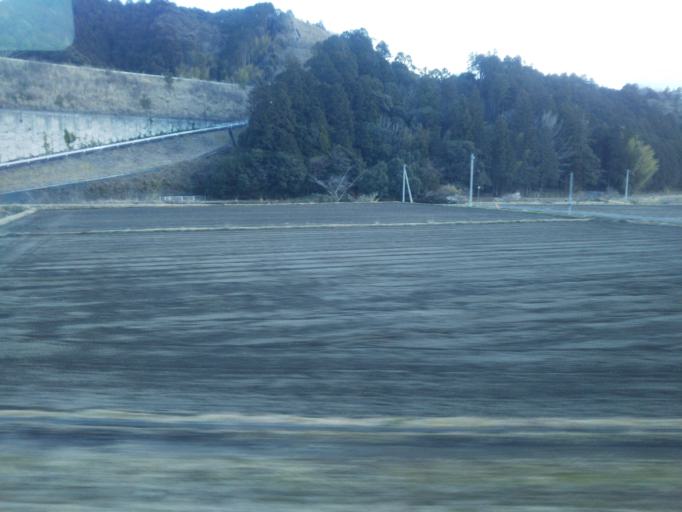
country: JP
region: Kochi
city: Susaki
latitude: 33.2770
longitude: 133.1797
